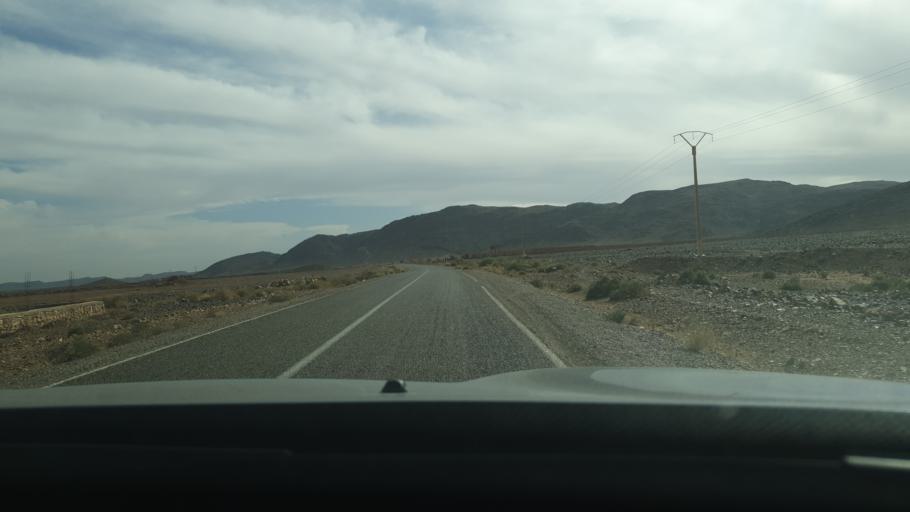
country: MA
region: Meknes-Tafilalet
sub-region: Errachidia
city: Fezna
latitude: 31.5302
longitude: -4.6388
